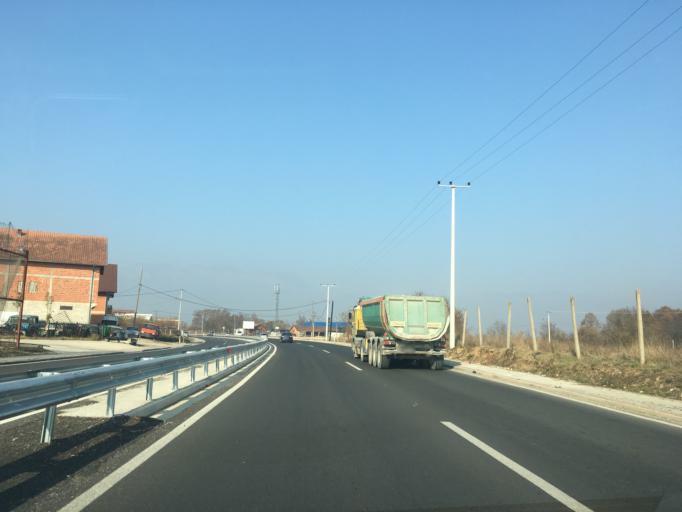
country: XK
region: Pec
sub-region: Komuna e Pejes
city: Dubova (Driloni)
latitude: 42.6530
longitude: 20.4015
